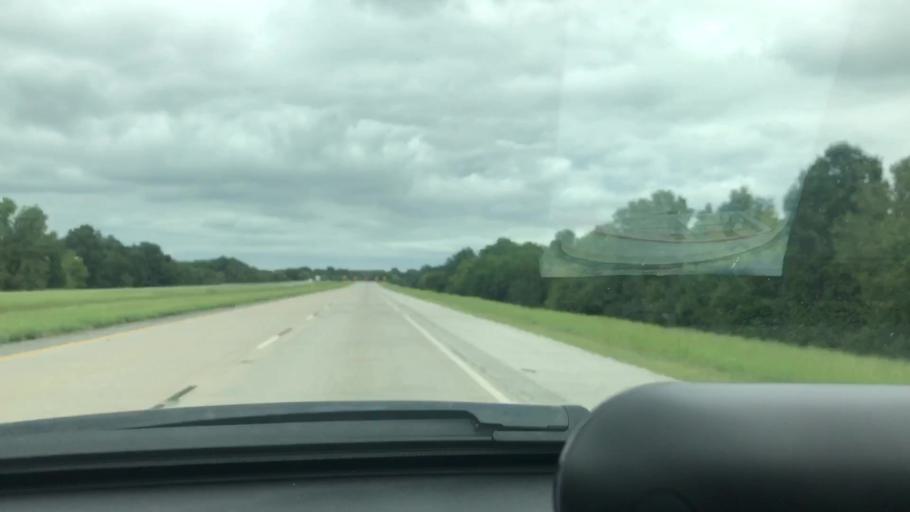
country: US
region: Oklahoma
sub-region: Wagoner County
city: Wagoner
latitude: 35.9028
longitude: -95.4026
